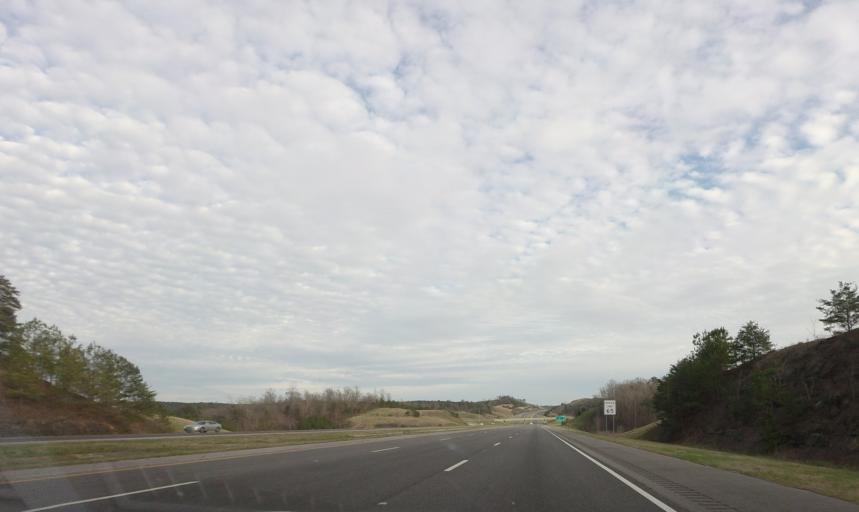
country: US
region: Alabama
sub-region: Jefferson County
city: Forestdale
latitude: 33.5979
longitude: -86.8951
